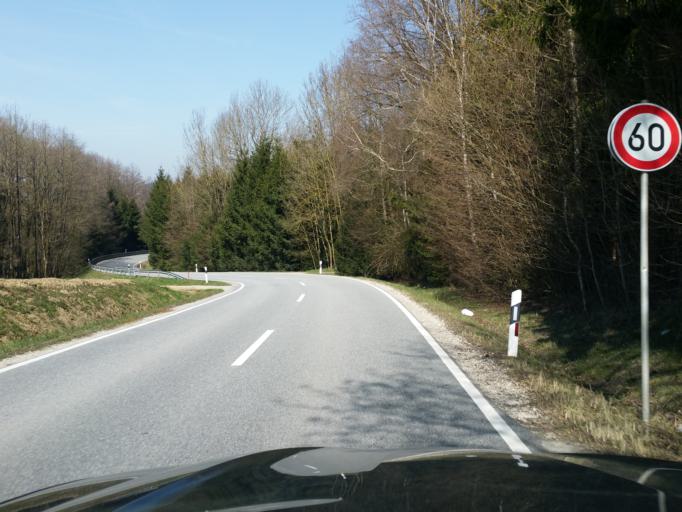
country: DE
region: Bavaria
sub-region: Upper Bavaria
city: Kirchberg
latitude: 48.4444
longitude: 12.0560
